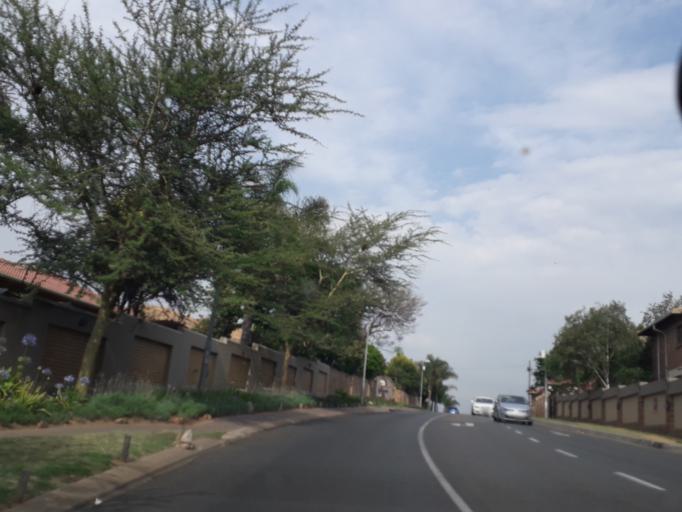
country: ZA
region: Gauteng
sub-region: City of Johannesburg Metropolitan Municipality
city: Roodepoort
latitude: -26.0956
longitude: 27.9306
